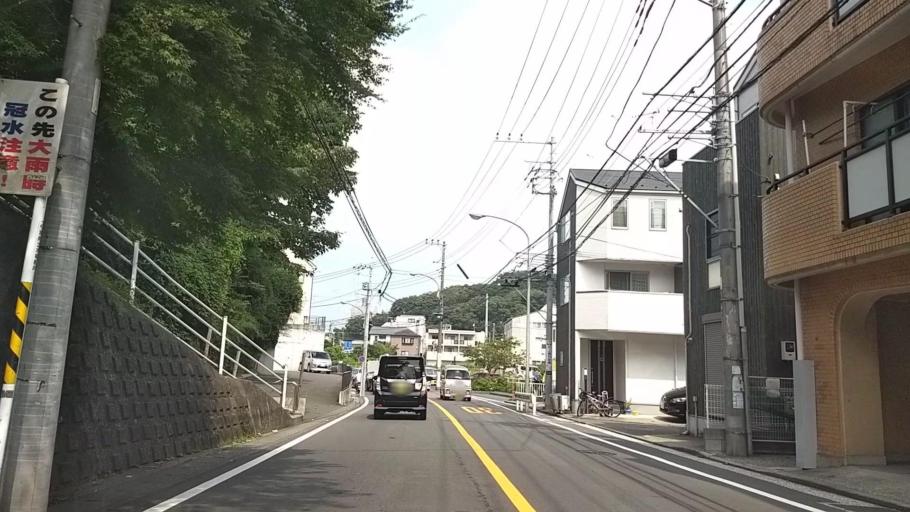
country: JP
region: Kanagawa
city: Yokohama
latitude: 35.4184
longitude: 139.5627
